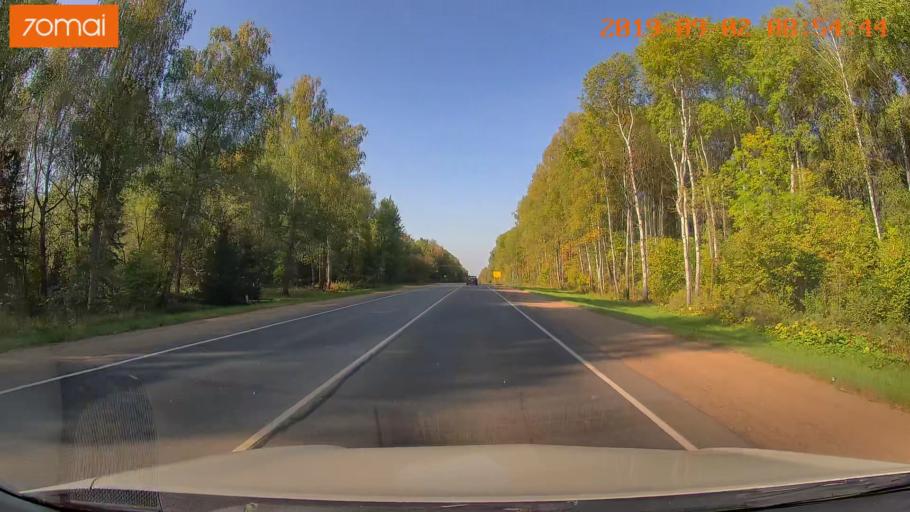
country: RU
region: Kaluga
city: Medyn'
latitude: 54.9594
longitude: 35.8330
